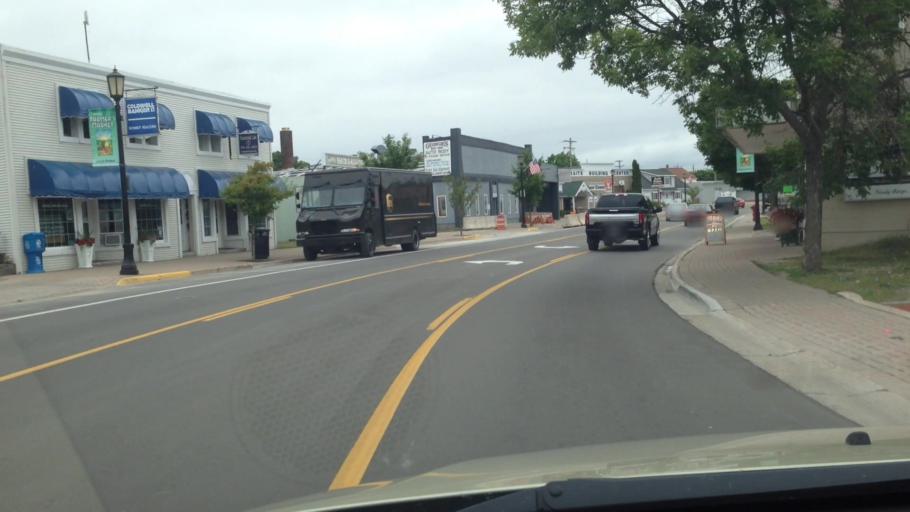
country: US
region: Michigan
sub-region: Mackinac County
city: Saint Ignace
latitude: 45.8694
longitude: -84.7297
